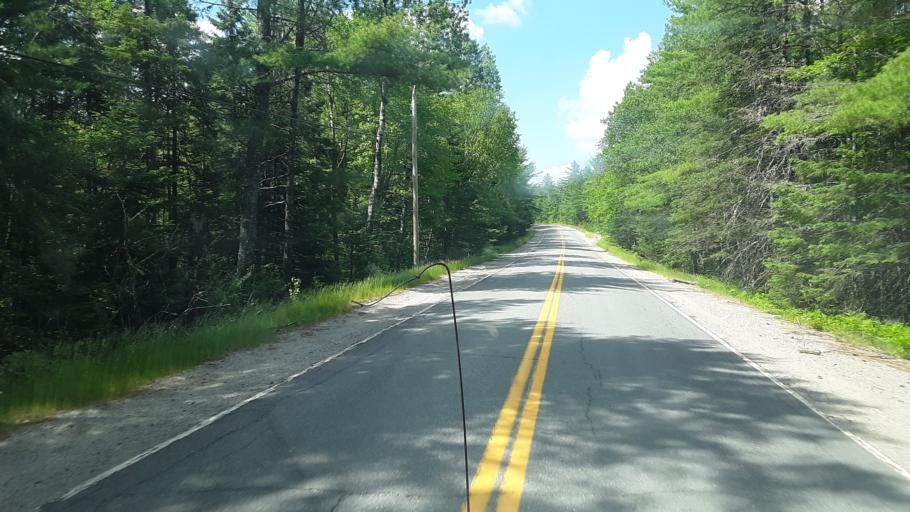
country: US
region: Maine
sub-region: Washington County
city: Machias
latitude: 44.8835
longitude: -67.6220
